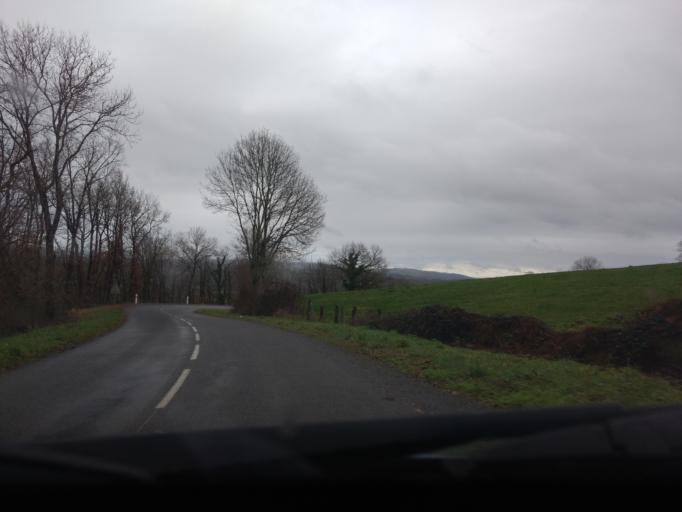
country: FR
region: Midi-Pyrenees
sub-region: Departement de l'Aveyron
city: Livinhac-le-Haut
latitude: 44.6190
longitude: 2.2029
